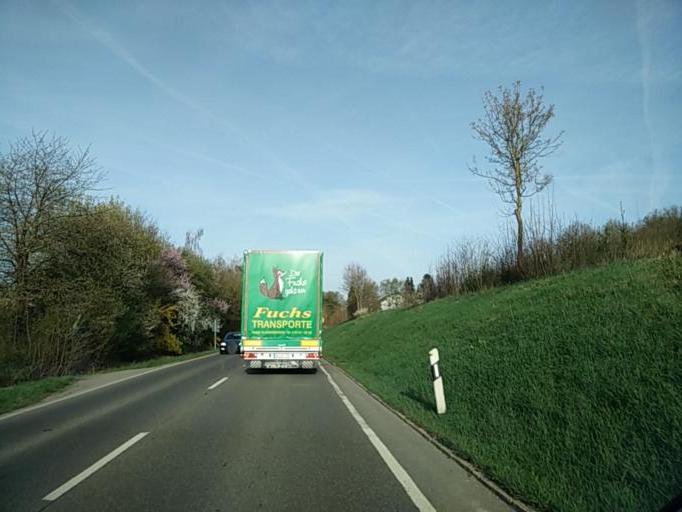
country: DE
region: Baden-Wuerttemberg
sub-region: Tuebingen Region
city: Tuebingen
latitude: 48.5241
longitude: 8.9933
